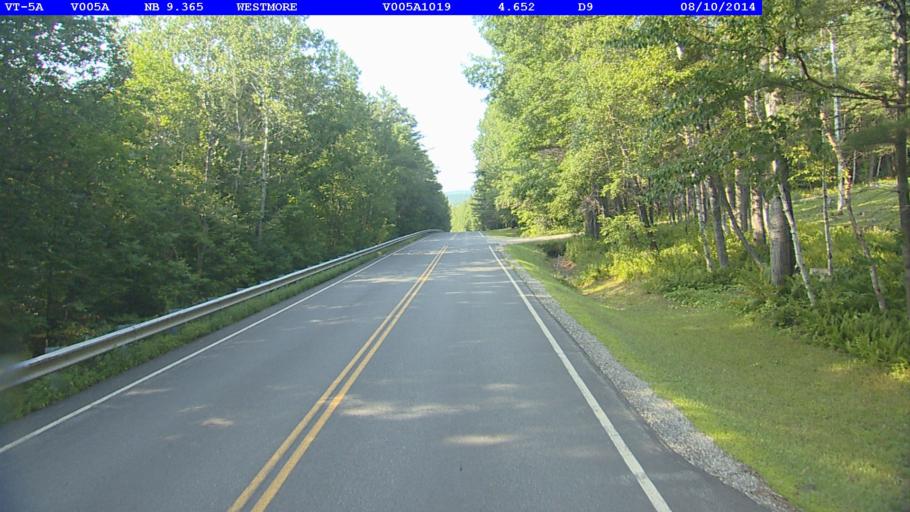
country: US
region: Vermont
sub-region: Caledonia County
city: Lyndonville
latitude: 44.7575
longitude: -72.0522
